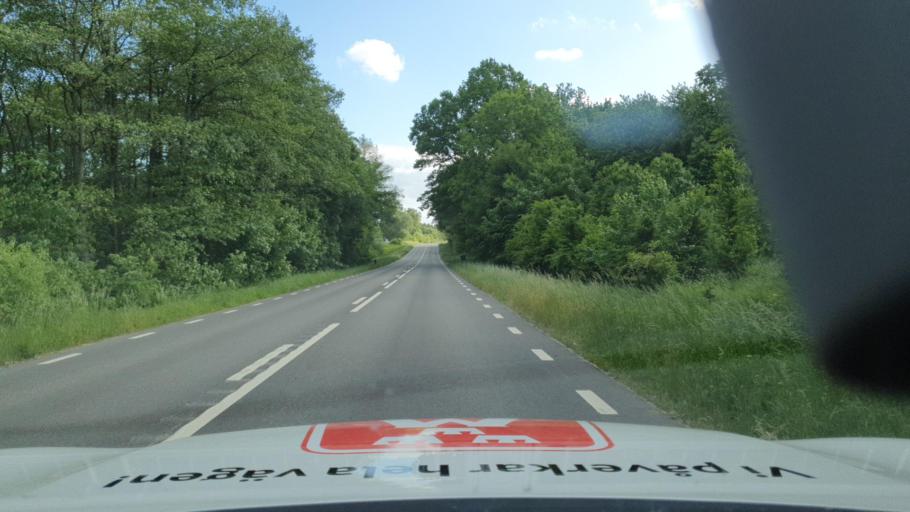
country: SE
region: Skane
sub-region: Simrishamns Kommun
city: Kivik
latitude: 55.5976
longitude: 14.1342
